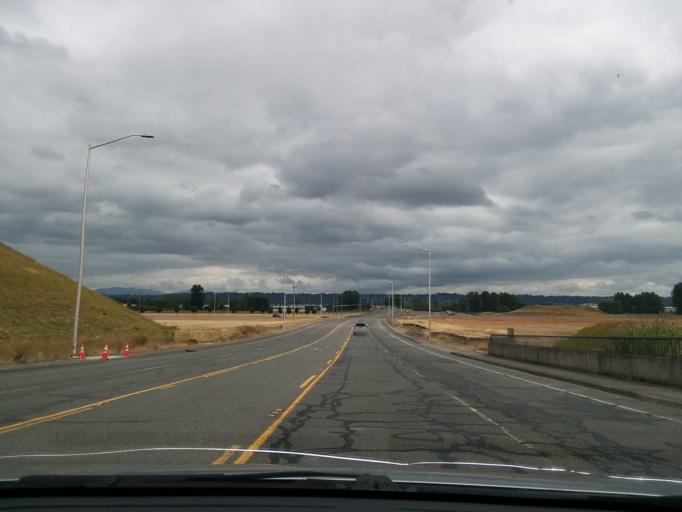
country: US
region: Washington
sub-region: King County
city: SeaTac
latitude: 47.4230
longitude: -122.2749
